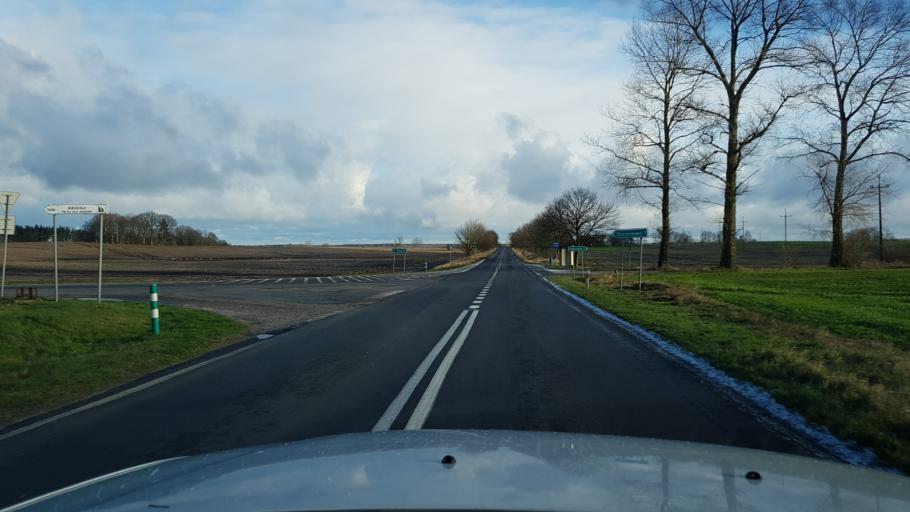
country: PL
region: West Pomeranian Voivodeship
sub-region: Powiat kolobrzeski
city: Grzybowo
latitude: 54.0830
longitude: 15.4508
